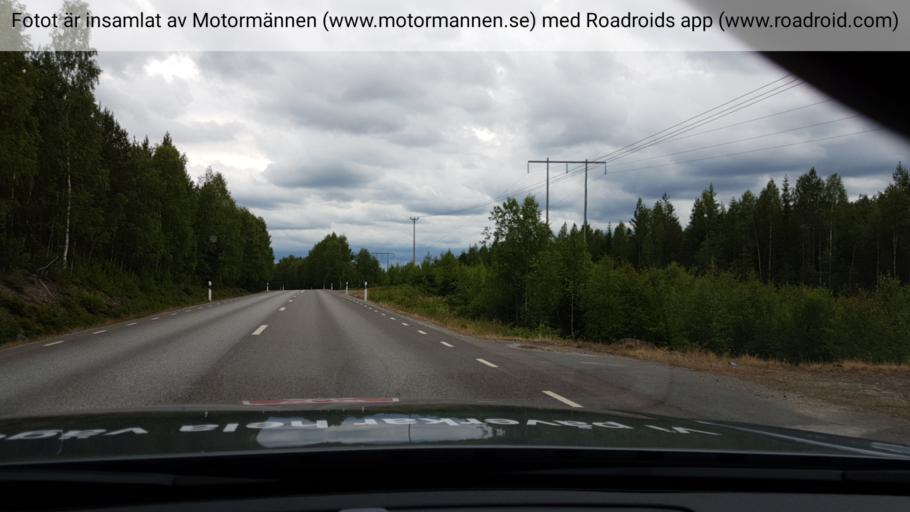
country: SE
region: Vaestmanland
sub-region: Skinnskattebergs Kommun
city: Skinnskatteberg
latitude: 59.8521
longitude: 15.6630
